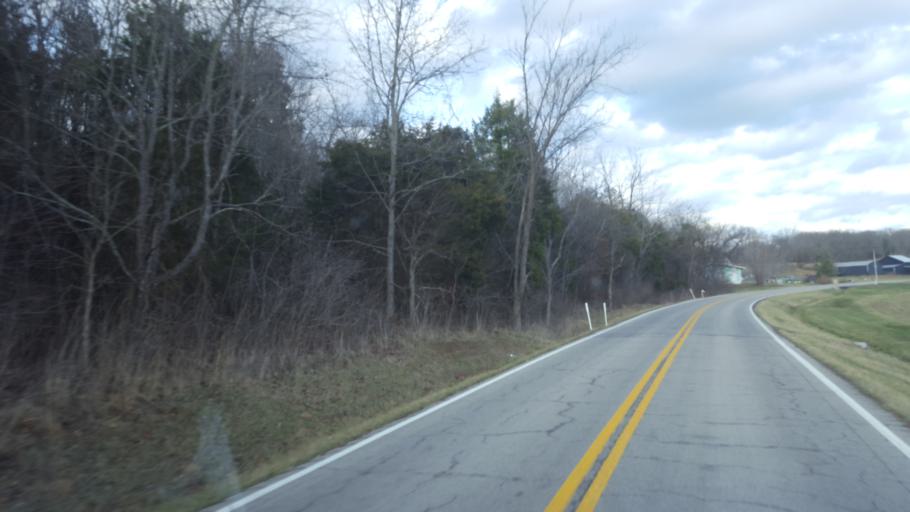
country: US
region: Kentucky
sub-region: Robertson County
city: Mount Olivet
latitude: 38.4622
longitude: -84.0311
